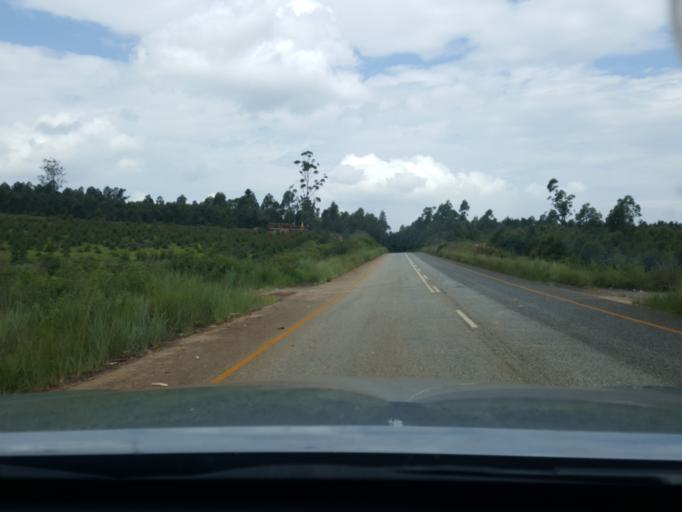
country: ZA
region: Mpumalanga
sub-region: Ehlanzeni District
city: White River
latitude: -25.1805
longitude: 30.8803
